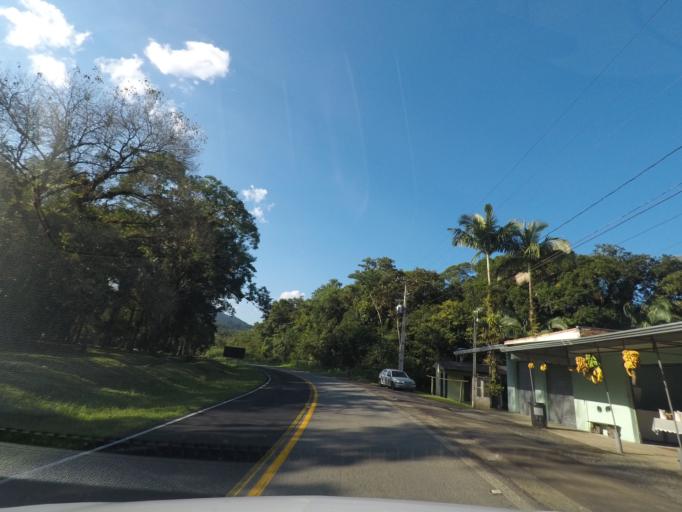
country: BR
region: Parana
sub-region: Antonina
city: Antonina
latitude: -25.3929
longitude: -48.8617
